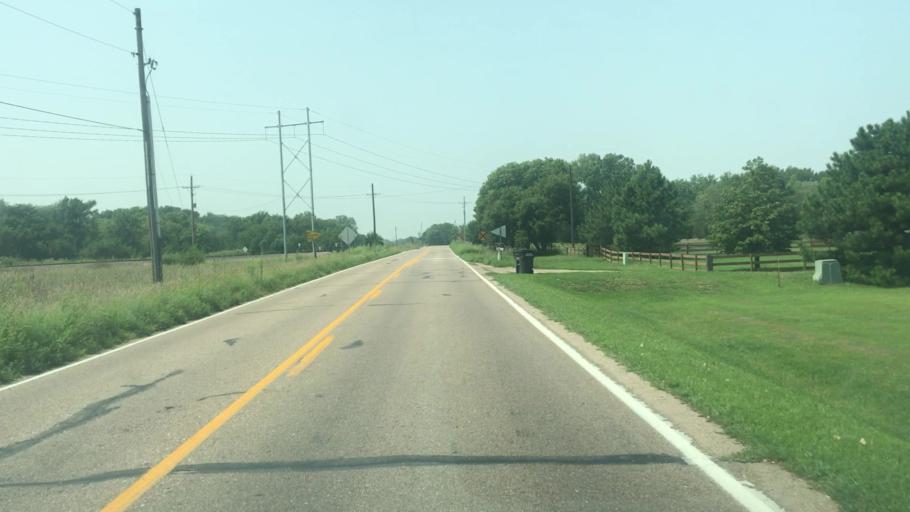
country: US
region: Nebraska
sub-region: Hall County
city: Grand Island
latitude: 40.9160
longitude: -98.3042
